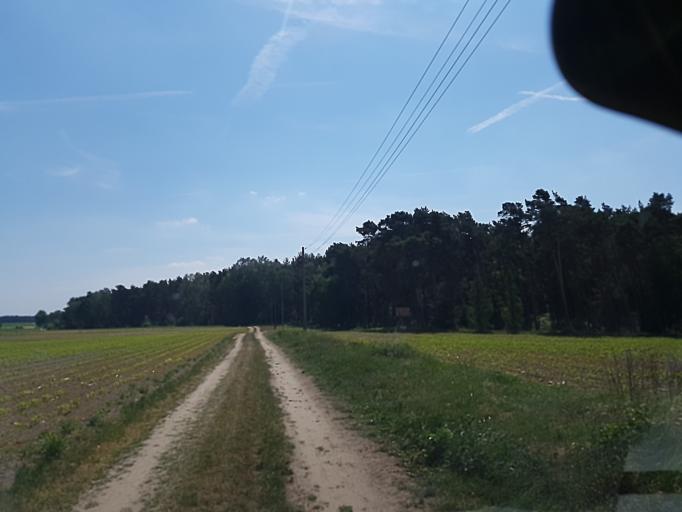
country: DE
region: Brandenburg
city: Gorzke
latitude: 52.0983
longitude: 12.3515
